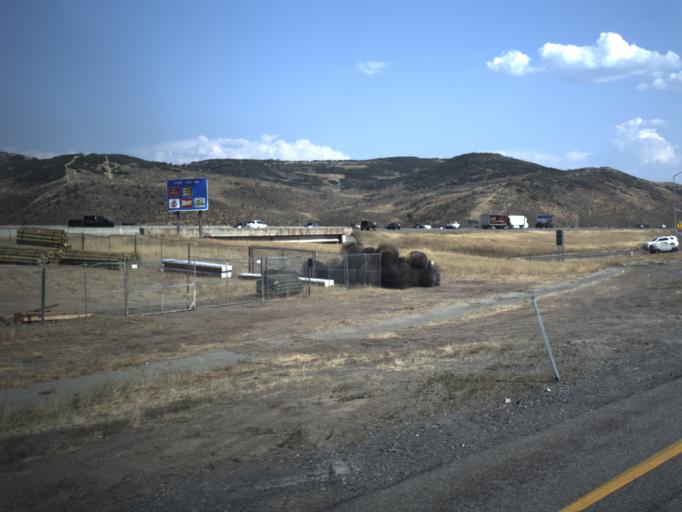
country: US
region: Utah
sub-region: Summit County
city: Summit Park
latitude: 40.7536
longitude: -111.5735
